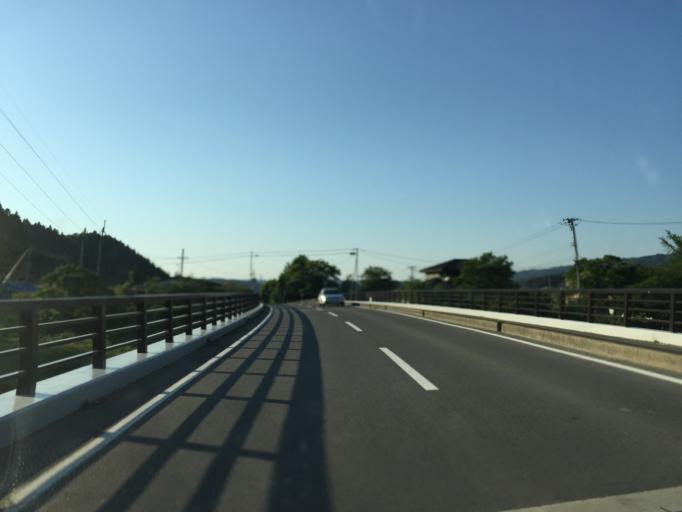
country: JP
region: Ibaraki
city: Daigo
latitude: 36.9463
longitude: 140.4402
